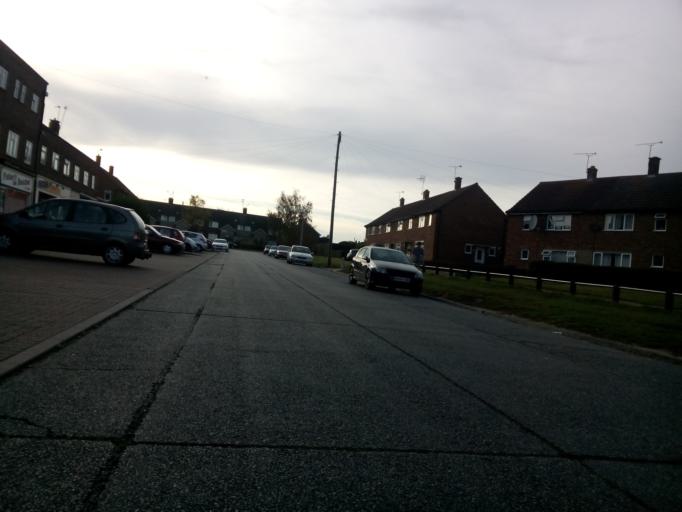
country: GB
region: England
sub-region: Suffolk
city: Ipswich
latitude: 52.0802
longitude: 1.1374
